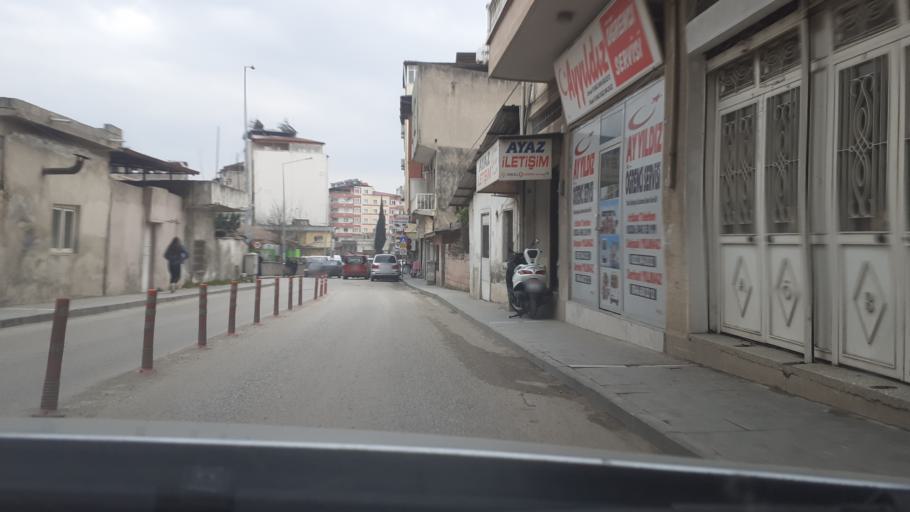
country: TR
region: Hatay
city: Kirikhan
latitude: 36.4973
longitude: 36.3564
